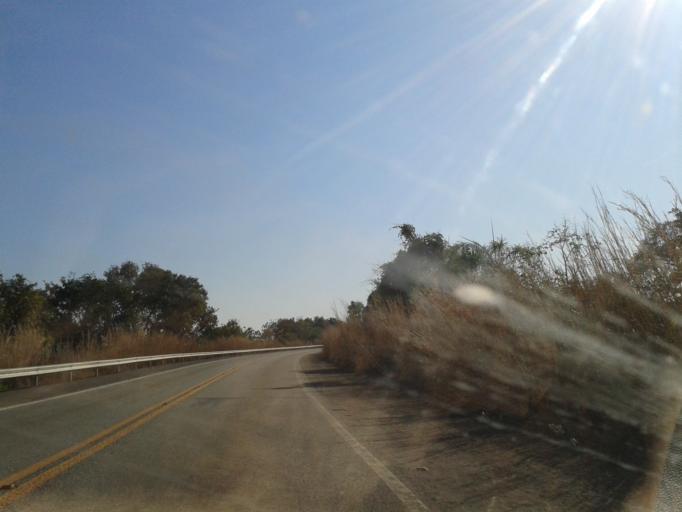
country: BR
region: Goias
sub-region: Mozarlandia
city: Mozarlandia
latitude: -14.9417
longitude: -50.5776
